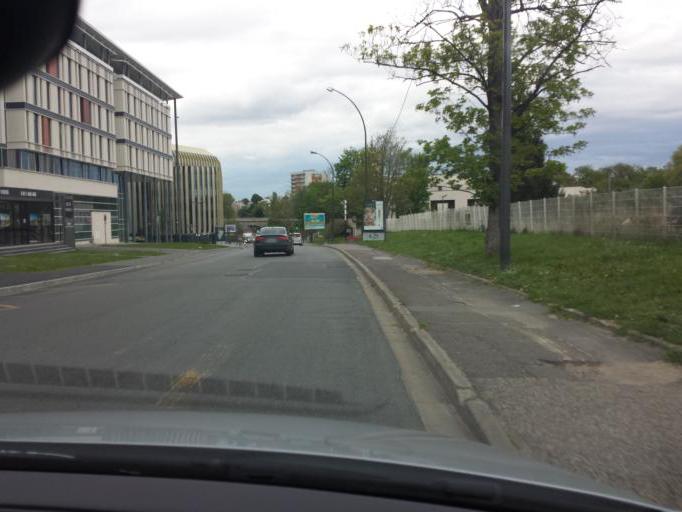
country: FR
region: Ile-de-France
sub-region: Departement de l'Essonne
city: Massy
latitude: 48.7256
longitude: 2.2703
